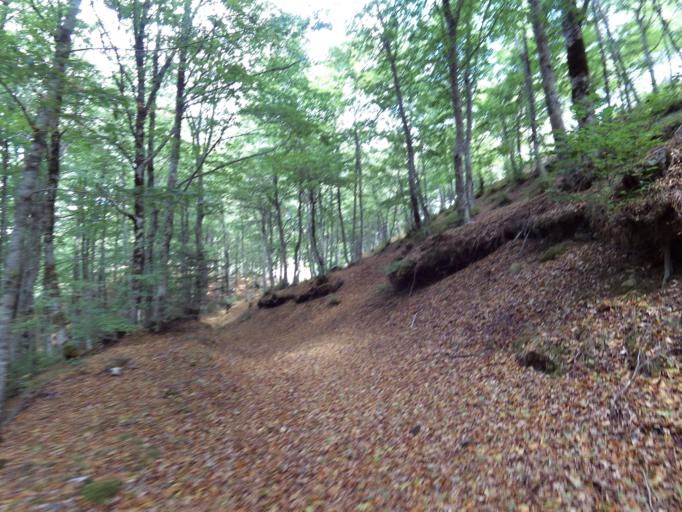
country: IT
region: Calabria
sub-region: Provincia di Vibo-Valentia
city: Mongiana
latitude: 38.5127
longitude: 16.3485
